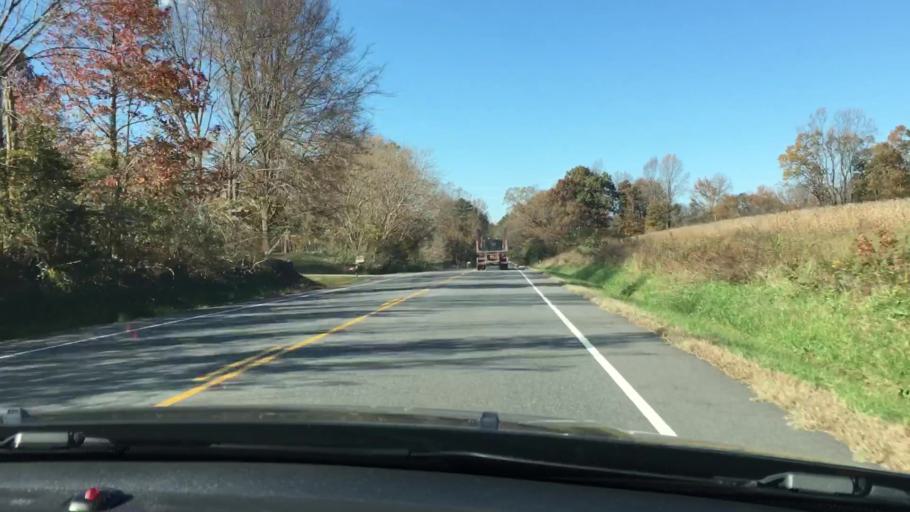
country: US
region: Virginia
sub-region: Hanover County
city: Hanover
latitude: 37.8048
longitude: -77.2650
